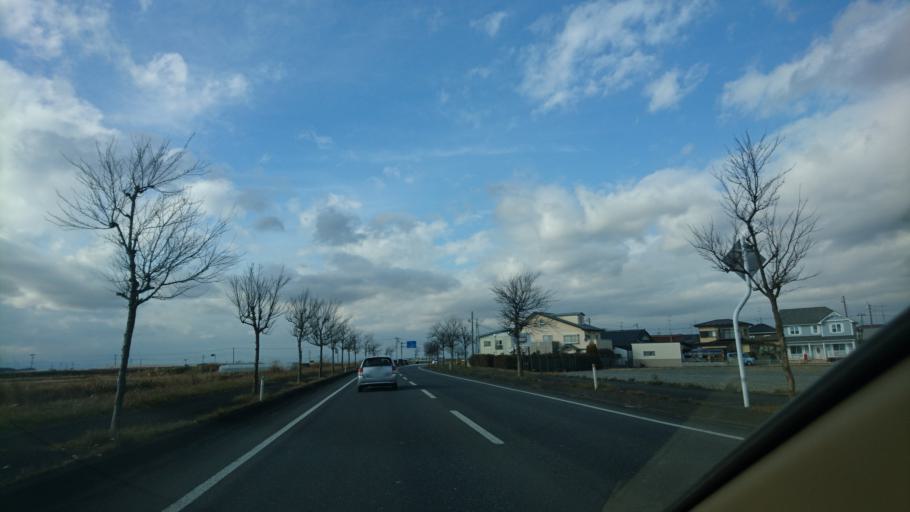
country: JP
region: Miyagi
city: Wakuya
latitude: 38.5326
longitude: 141.1248
